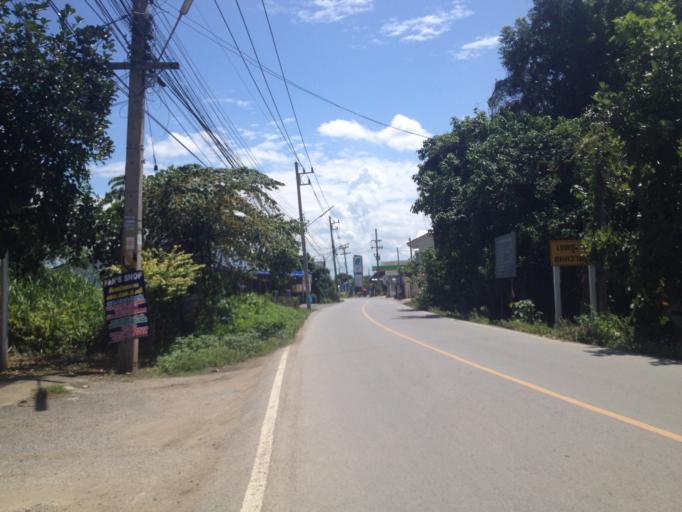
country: TH
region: Chiang Mai
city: Hang Dong
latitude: 18.6603
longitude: 98.9214
